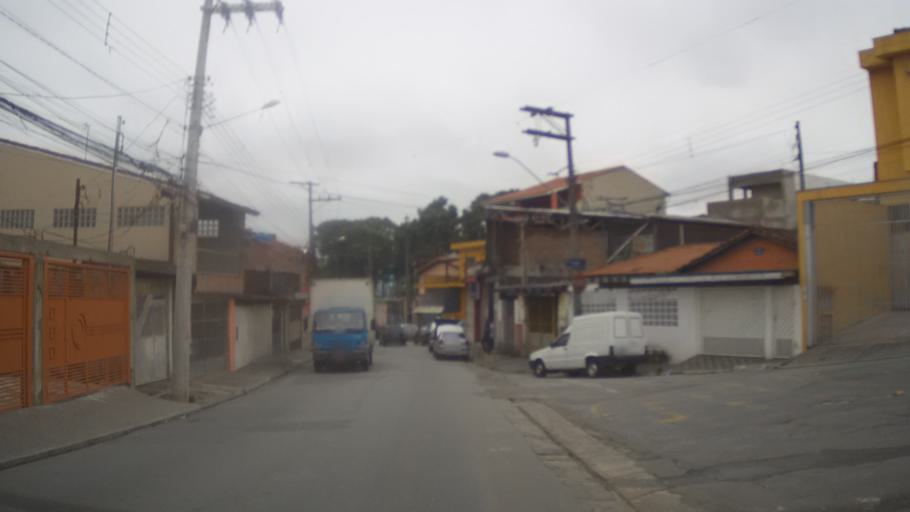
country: BR
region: Sao Paulo
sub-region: Guarulhos
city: Guarulhos
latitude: -23.4328
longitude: -46.5165
